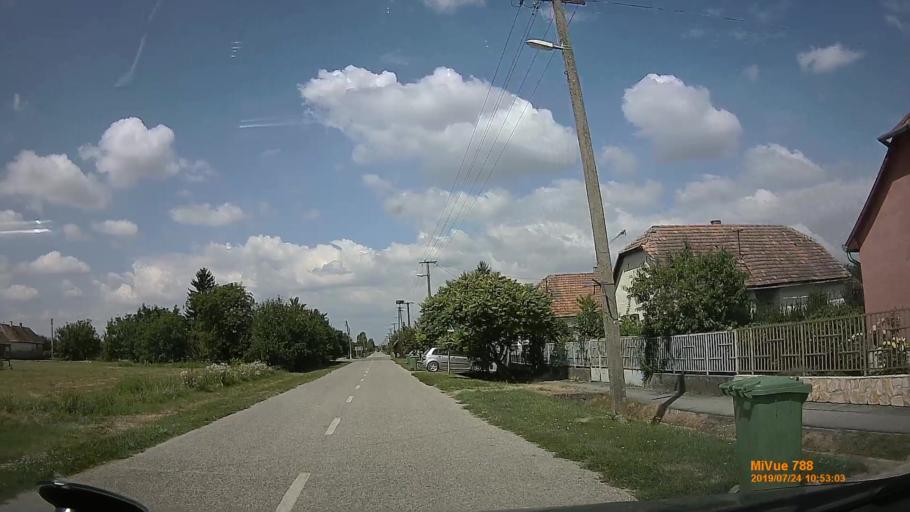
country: HU
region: Szabolcs-Szatmar-Bereg
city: Tarpa
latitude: 48.1971
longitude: 22.5486
